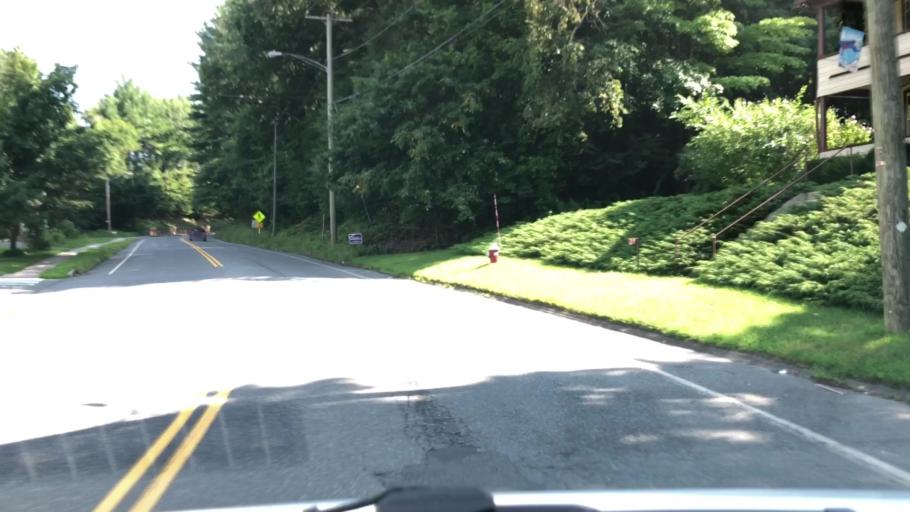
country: US
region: Massachusetts
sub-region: Franklin County
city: Turners Falls
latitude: 42.6031
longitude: -72.5517
